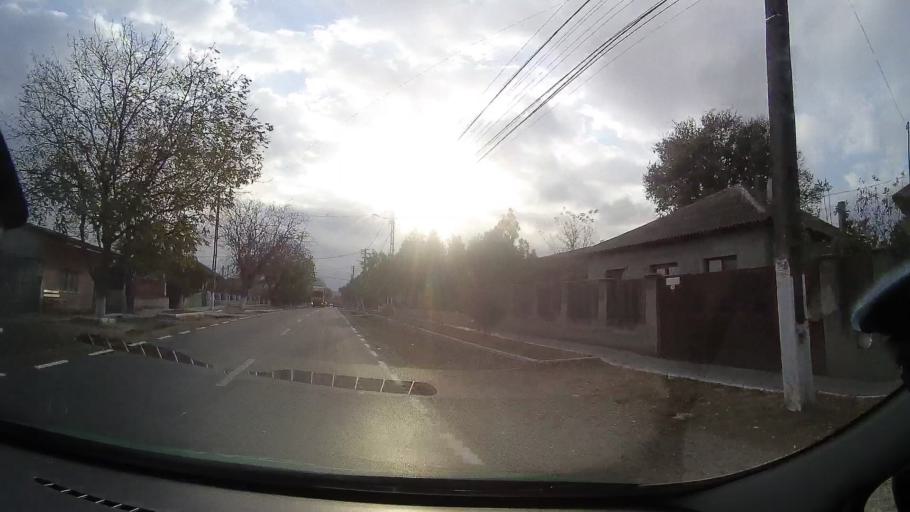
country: RO
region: Constanta
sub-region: Comuna Mircea Voda
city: Mircea Voda
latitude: 44.2811
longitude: 28.1764
